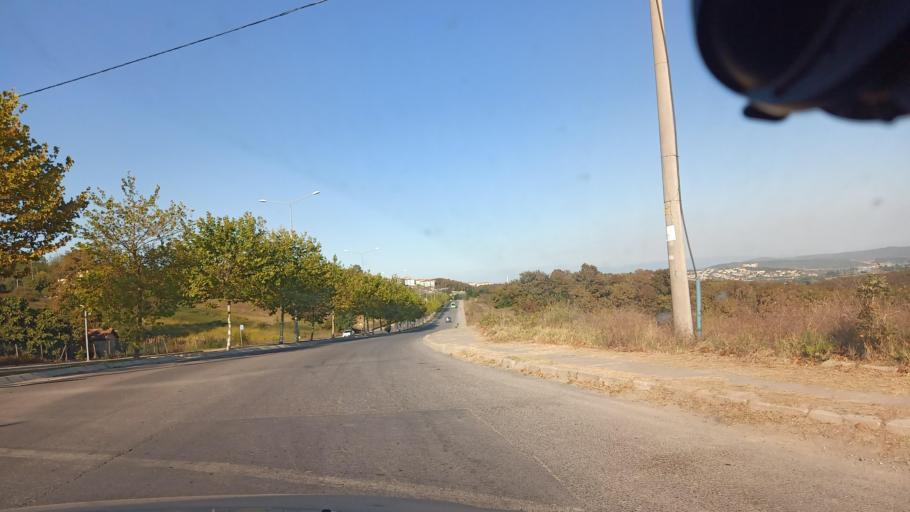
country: TR
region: Sakarya
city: Kazimpasa
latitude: 40.8498
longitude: 30.2798
